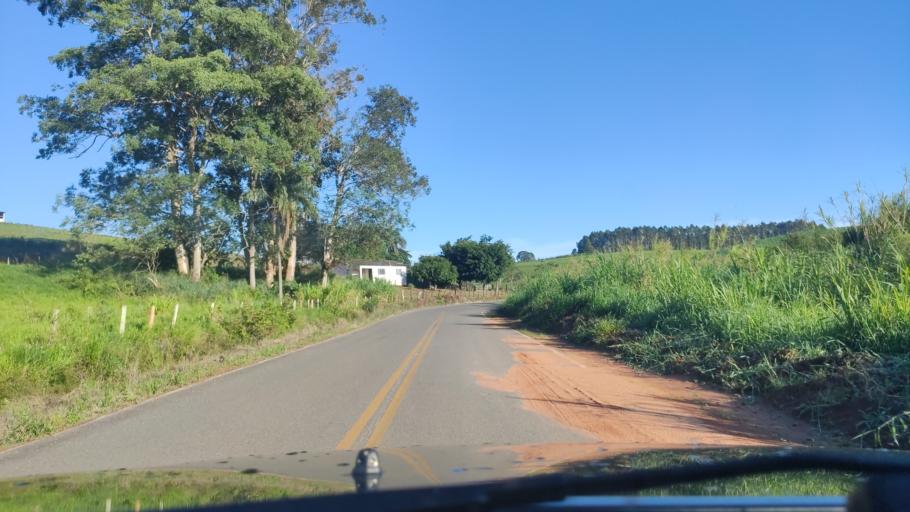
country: BR
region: Sao Paulo
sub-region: Serra Negra
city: Serra Negra
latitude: -22.5687
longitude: -46.6224
